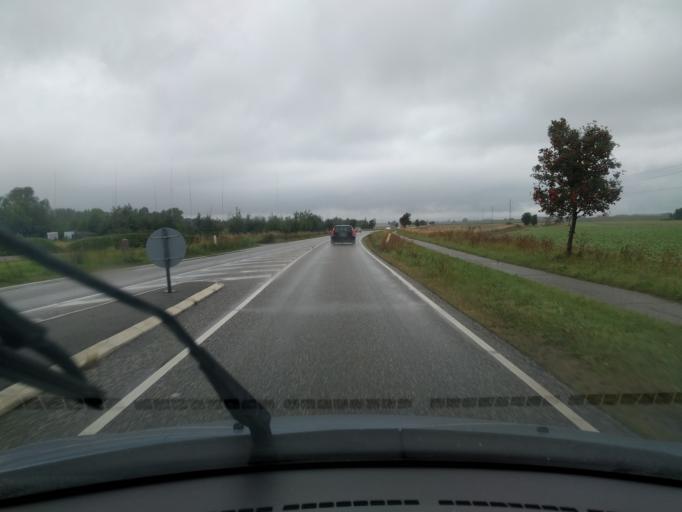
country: DK
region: Zealand
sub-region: Vordingborg Kommune
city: Neder Vindinge
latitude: 55.1139
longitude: 11.8189
